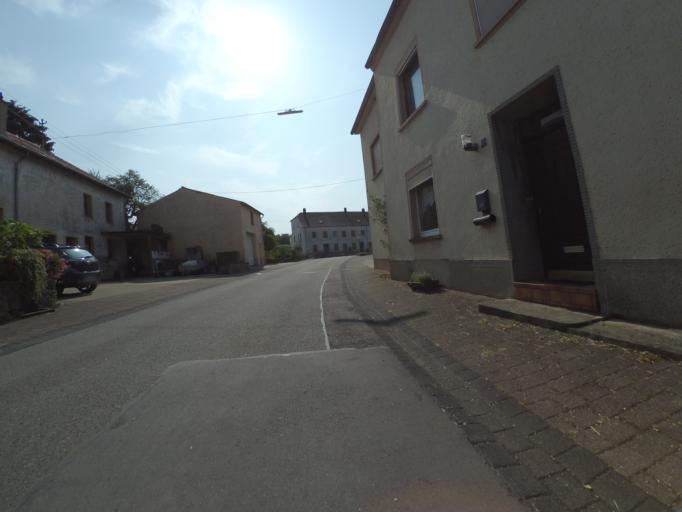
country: DE
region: Saarland
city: Perl
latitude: 49.5150
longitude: 6.4149
